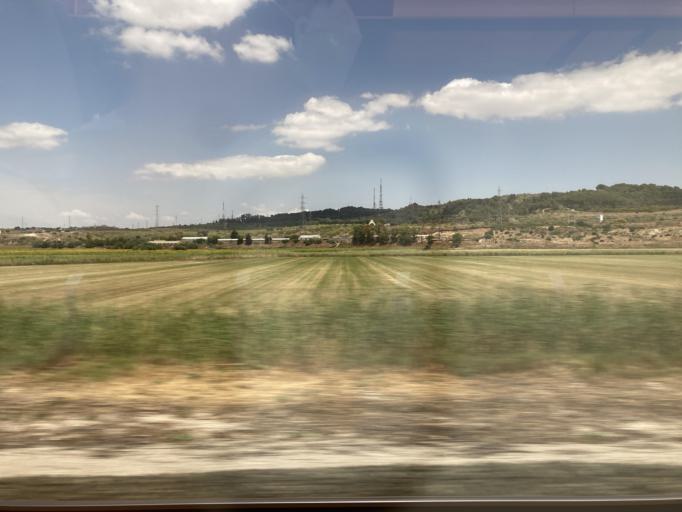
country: ES
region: Andalusia
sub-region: Provincia de Cadiz
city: Jerez de la Frontera
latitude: 36.6206
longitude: -6.1534
